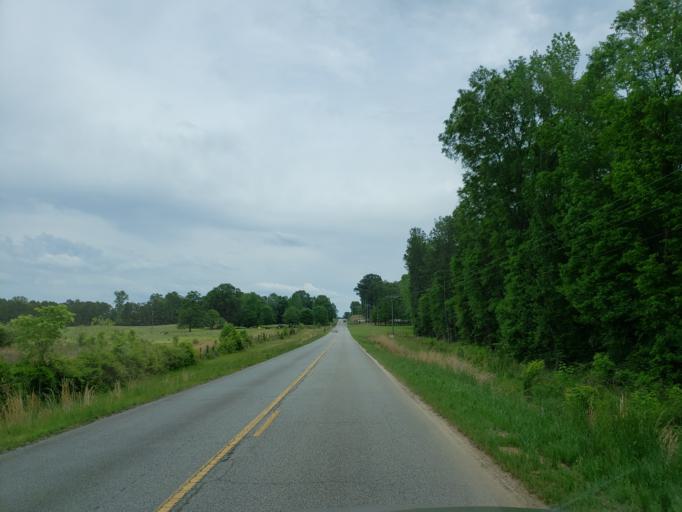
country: US
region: Georgia
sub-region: Bibb County
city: West Point
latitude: 32.8272
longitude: -83.8815
